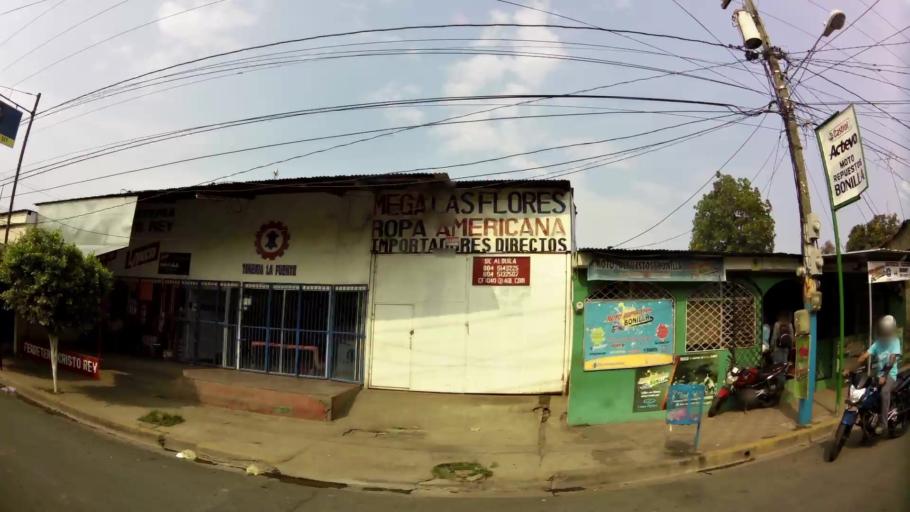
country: NI
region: Masaya
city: Masaya
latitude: 11.9706
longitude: -86.0949
